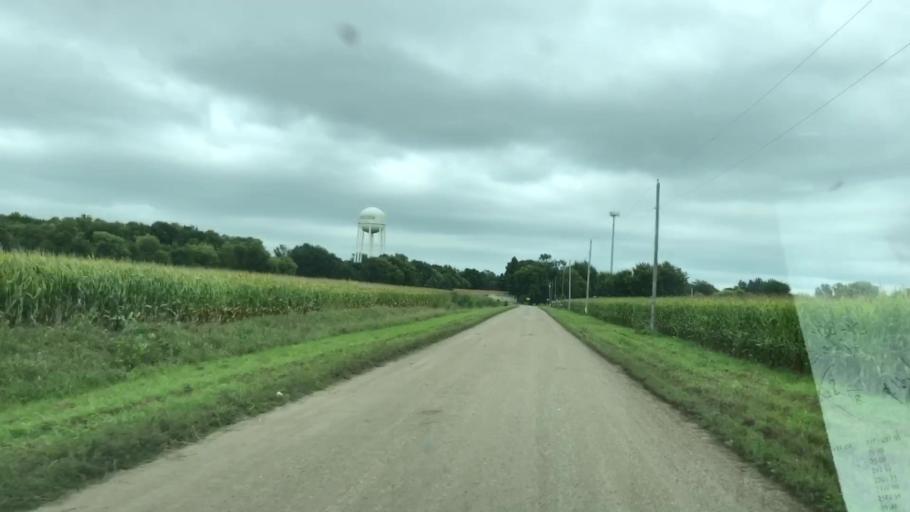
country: US
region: Iowa
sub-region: O'Brien County
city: Sheldon
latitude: 43.1751
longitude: -95.8537
